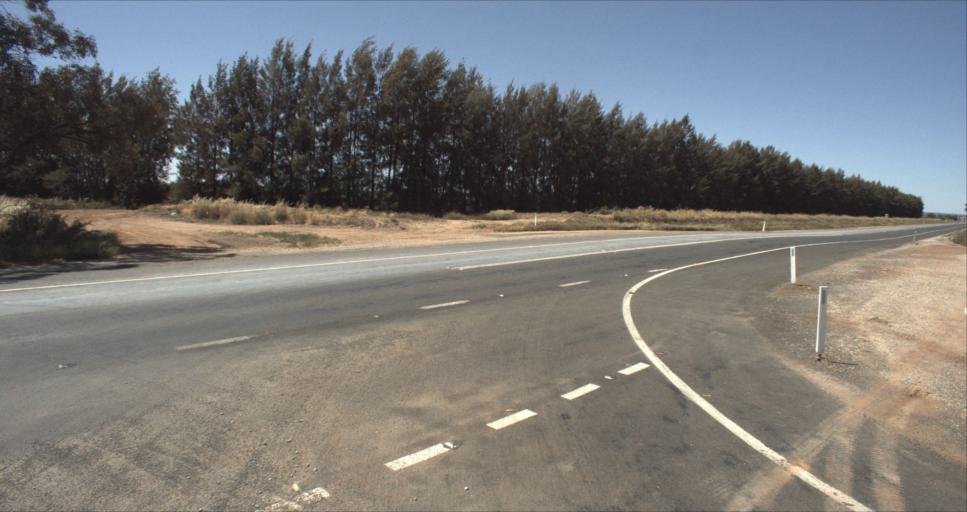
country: AU
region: New South Wales
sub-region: Leeton
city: Leeton
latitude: -34.5223
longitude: 146.3306
